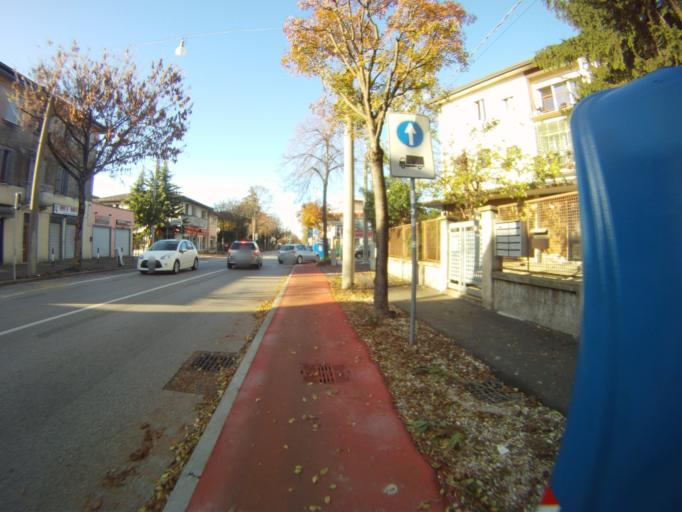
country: IT
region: Veneto
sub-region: Provincia di Padova
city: Padova
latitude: 45.3886
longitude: 11.8950
